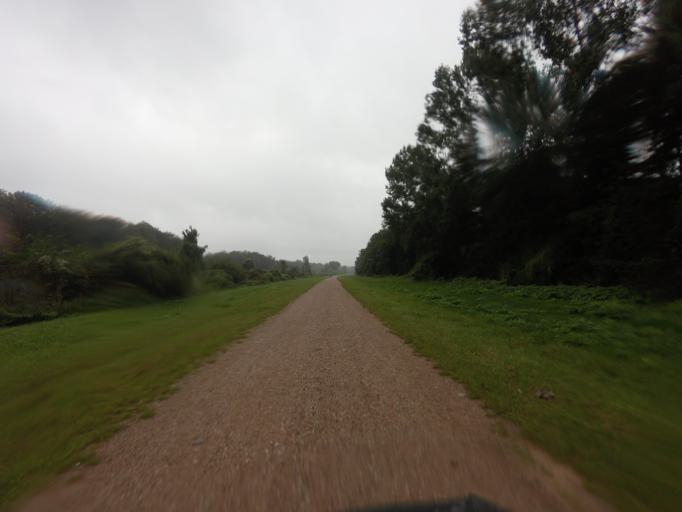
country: NL
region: North Holland
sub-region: Gemeente Huizen
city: Huizen
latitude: 52.3394
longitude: 5.2547
